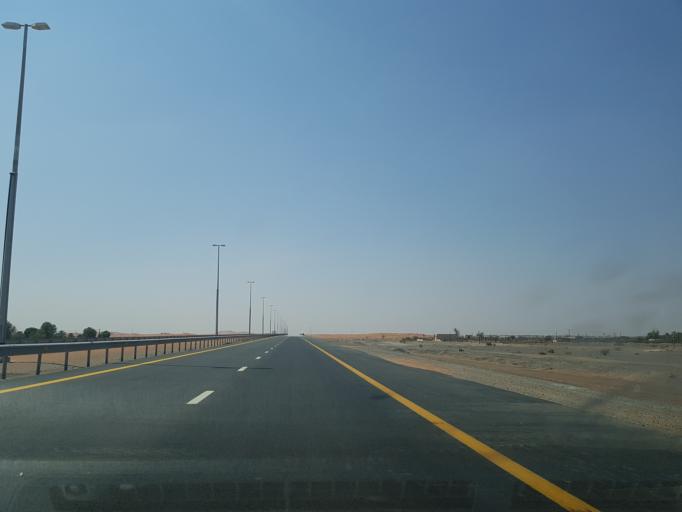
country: AE
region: Ash Shariqah
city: Adh Dhayd
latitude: 25.2377
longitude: 55.8957
